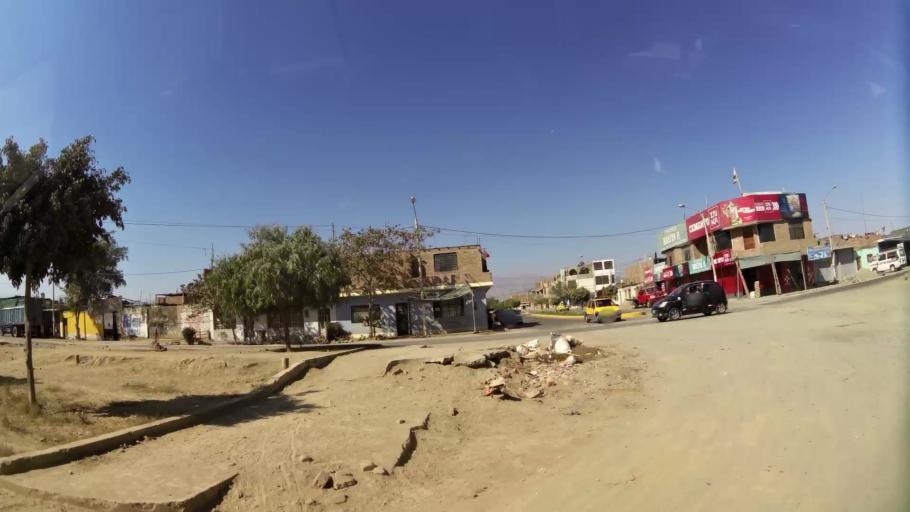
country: PE
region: Ica
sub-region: Provincia de Ica
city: La Tinguina
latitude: -14.0349
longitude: -75.7072
